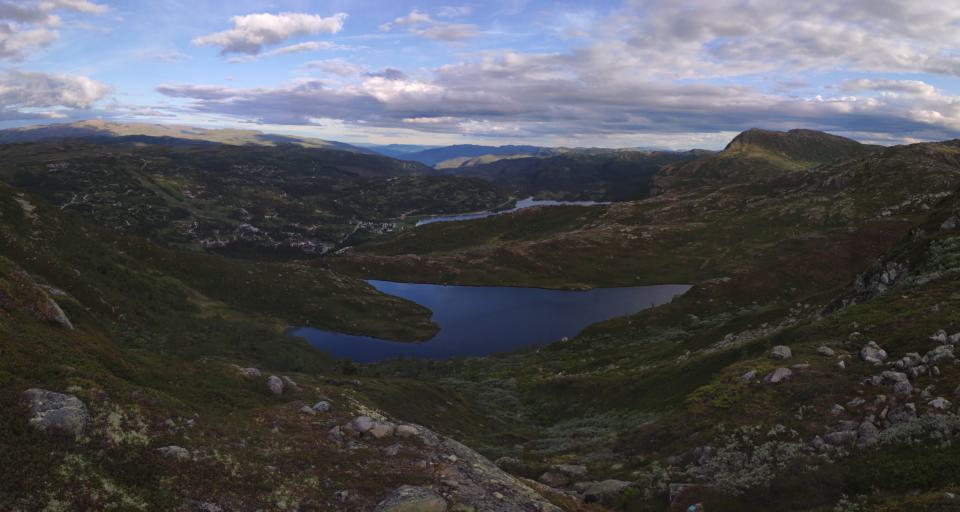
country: NO
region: Buskerud
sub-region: Nes
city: Nesbyen
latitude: 60.3535
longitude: 9.1681
